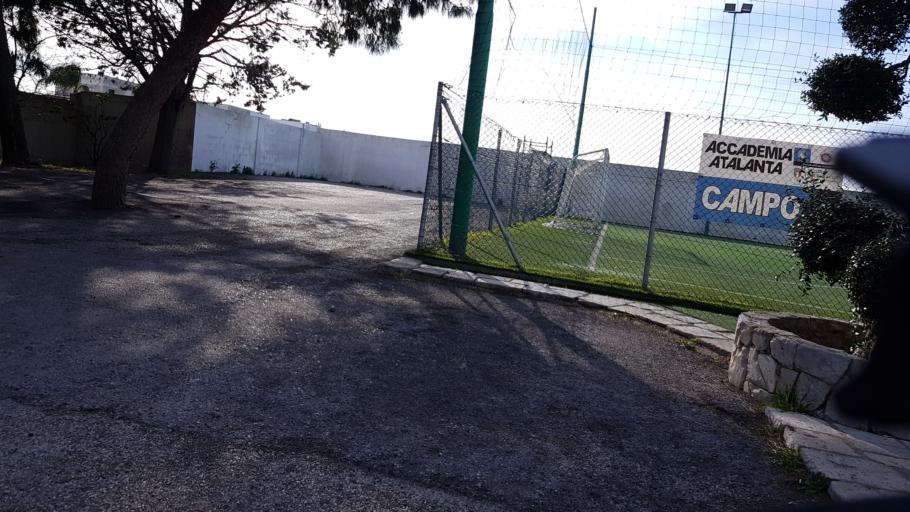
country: IT
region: Apulia
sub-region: Provincia di Brindisi
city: Brindisi
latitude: 40.6483
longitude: 17.9299
